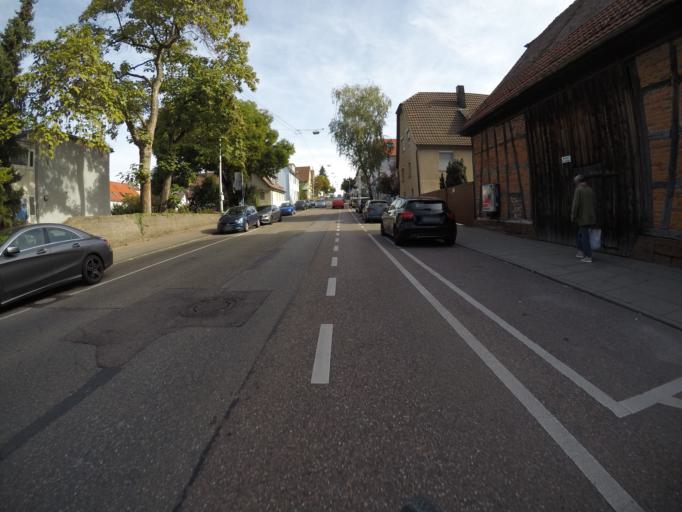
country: DE
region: Baden-Wuerttemberg
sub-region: Regierungsbezirk Stuttgart
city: Korntal
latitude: 48.8153
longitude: 9.1133
